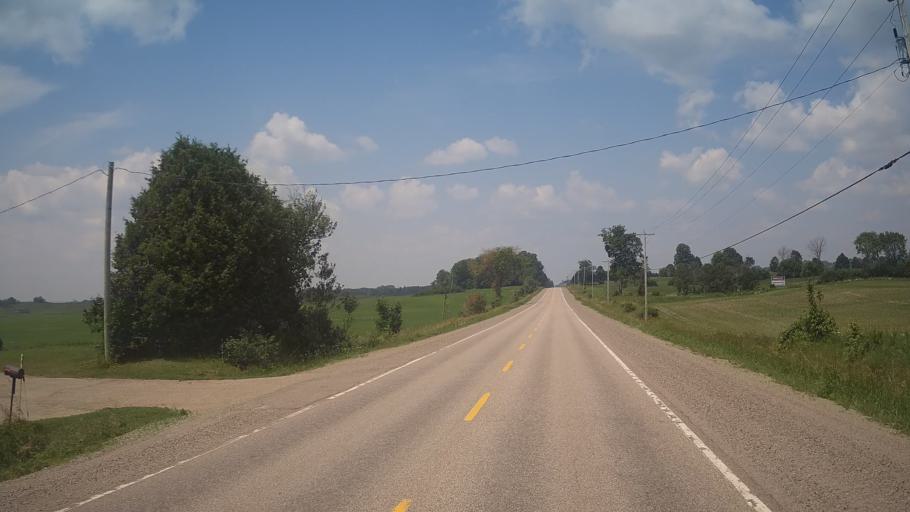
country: CA
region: Quebec
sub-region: Outaouais
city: Shawville
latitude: 45.5911
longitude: -76.4707
